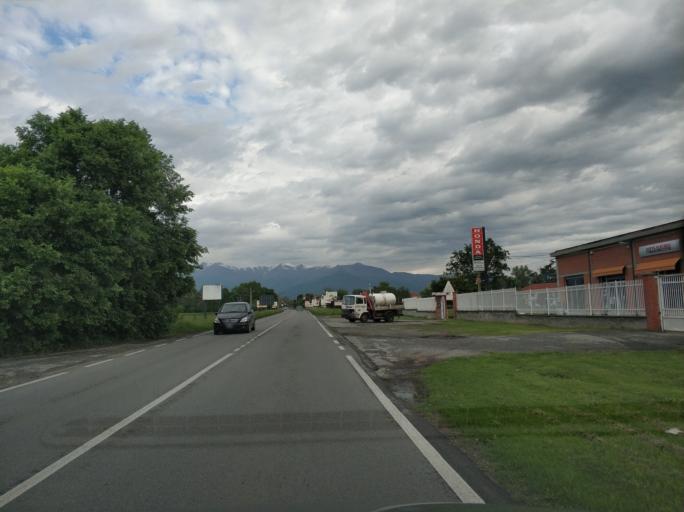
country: IT
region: Piedmont
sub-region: Provincia di Torino
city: San Maurizio
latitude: 45.2251
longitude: 7.6202
